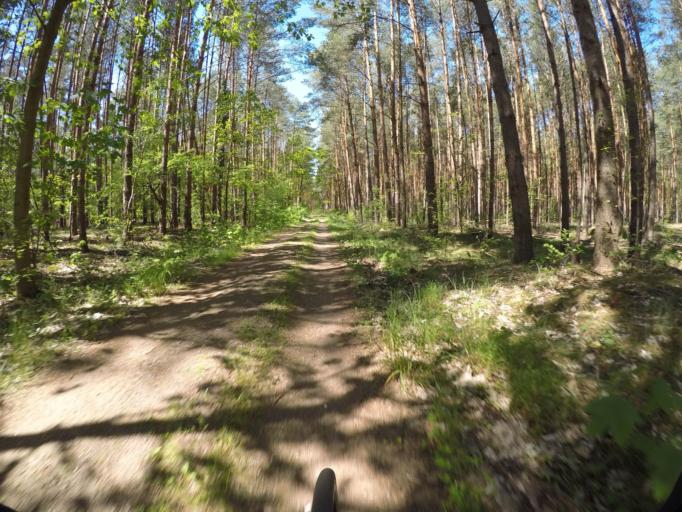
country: DE
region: Berlin
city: Kladow
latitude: 52.4537
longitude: 13.0895
